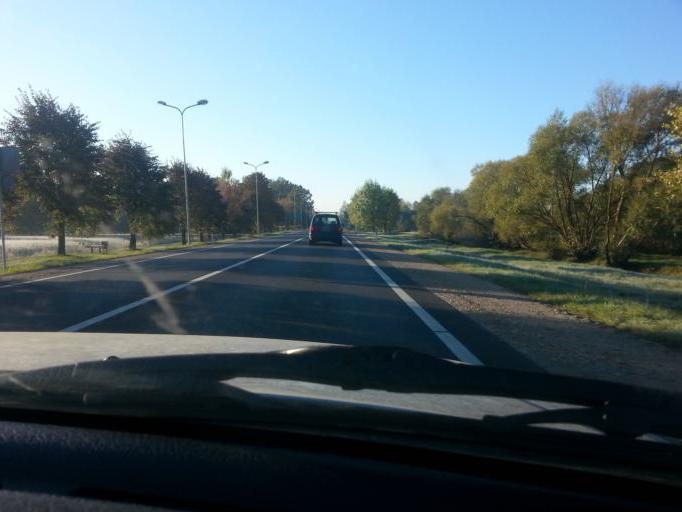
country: LT
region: Siauliu apskritis
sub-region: Joniskis
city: Joniskis
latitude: 56.4149
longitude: 23.6833
